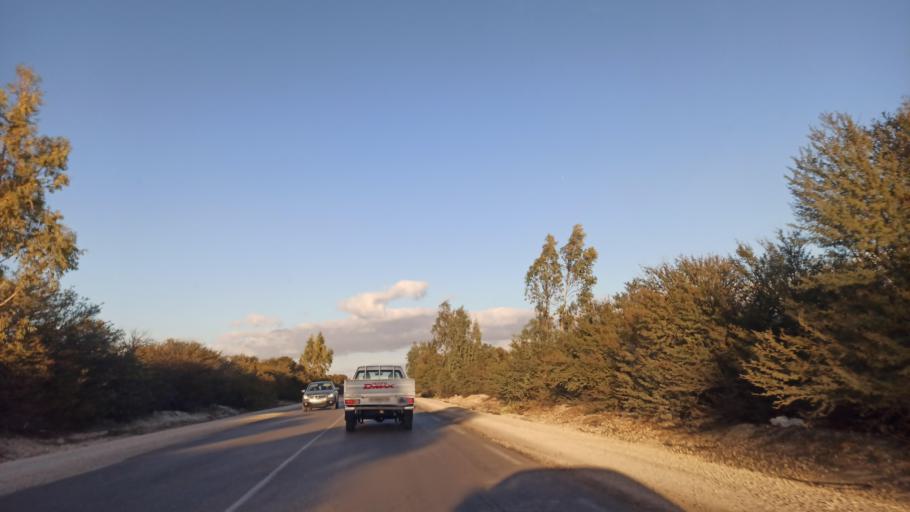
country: TN
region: Al Qayrawan
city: Sbikha
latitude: 35.8567
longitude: 10.2022
